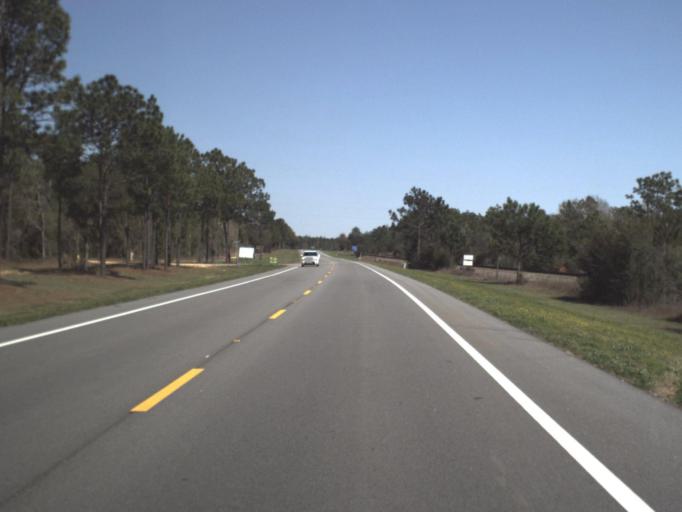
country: US
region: Florida
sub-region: Okaloosa County
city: Crestview
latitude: 30.7426
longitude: -86.3880
